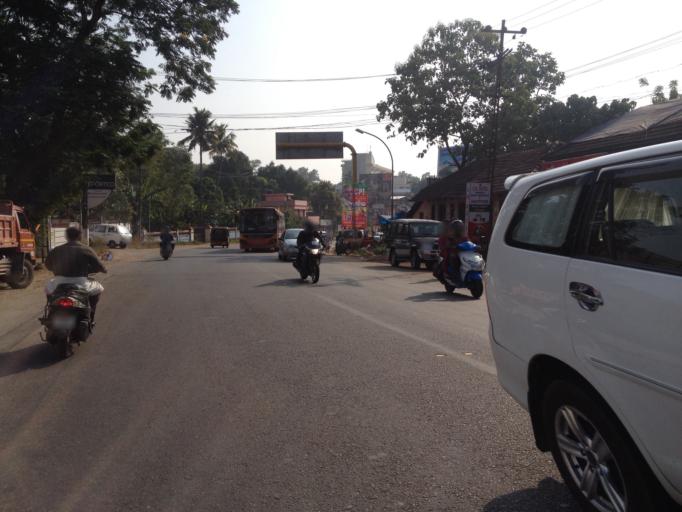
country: IN
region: Kerala
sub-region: Pattanamtitta
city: Adur
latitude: 9.1618
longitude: 76.7216
